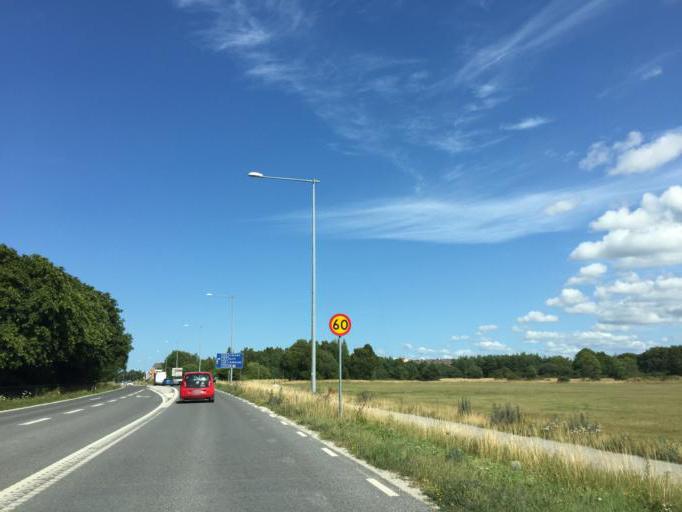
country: SE
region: Gotland
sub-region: Gotland
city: Vibble
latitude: 57.6189
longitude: 18.2736
